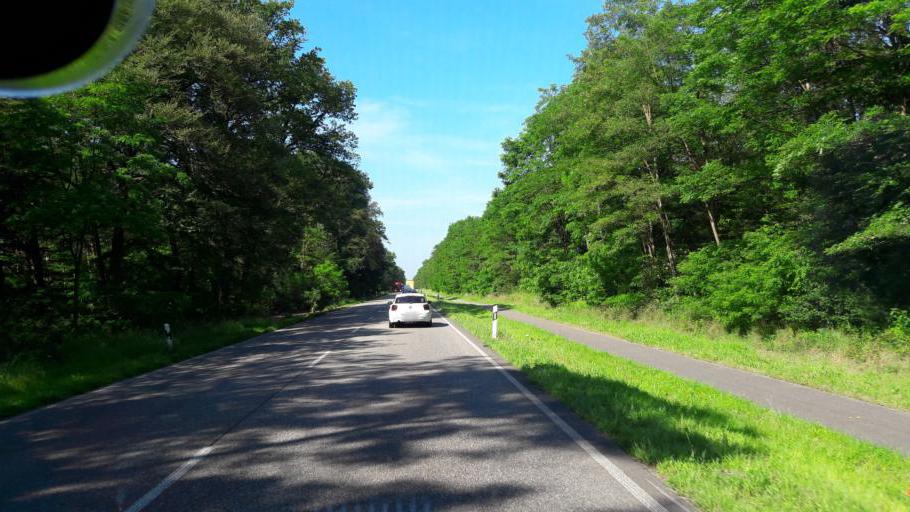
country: DE
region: Baden-Wuerttemberg
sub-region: Karlsruhe Region
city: Muggensturm
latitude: 48.8939
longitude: 8.2909
